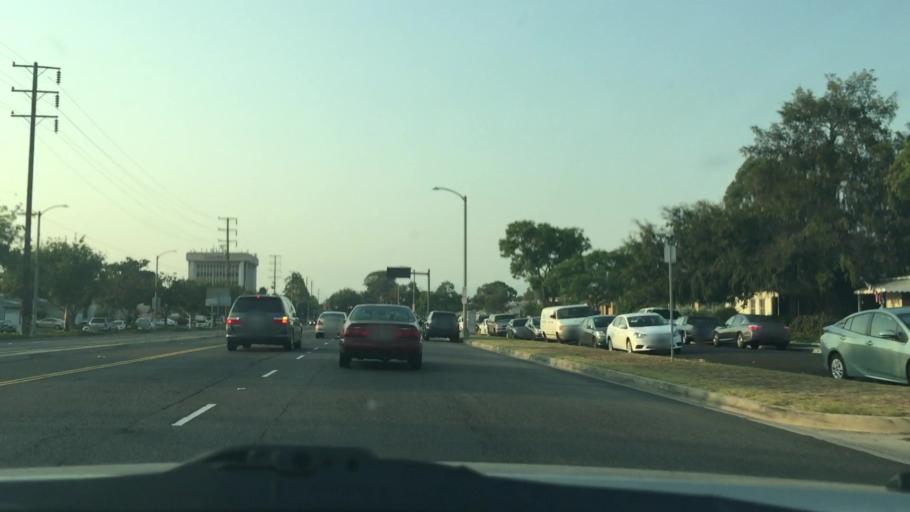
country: US
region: California
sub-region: Los Angeles County
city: Lakewood
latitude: 33.8426
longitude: -118.1435
